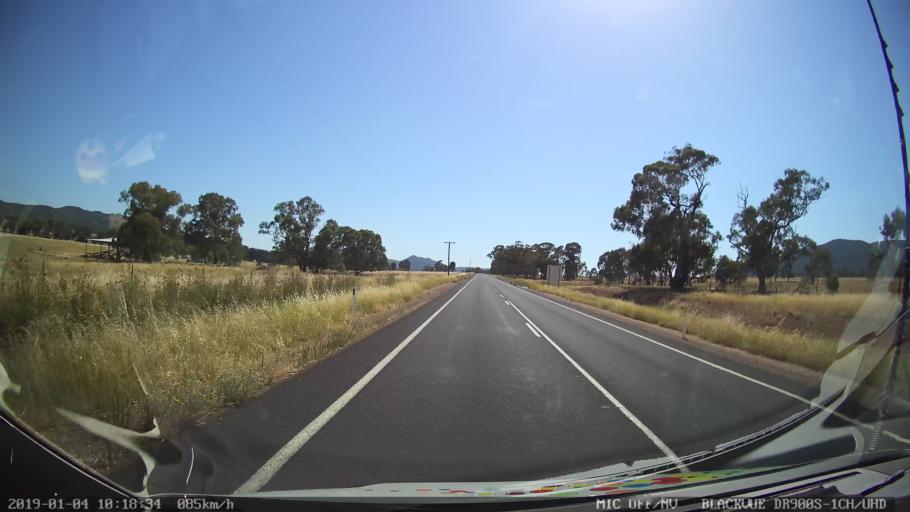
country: AU
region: New South Wales
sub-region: Cabonne
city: Canowindra
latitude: -33.3814
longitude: 148.4685
